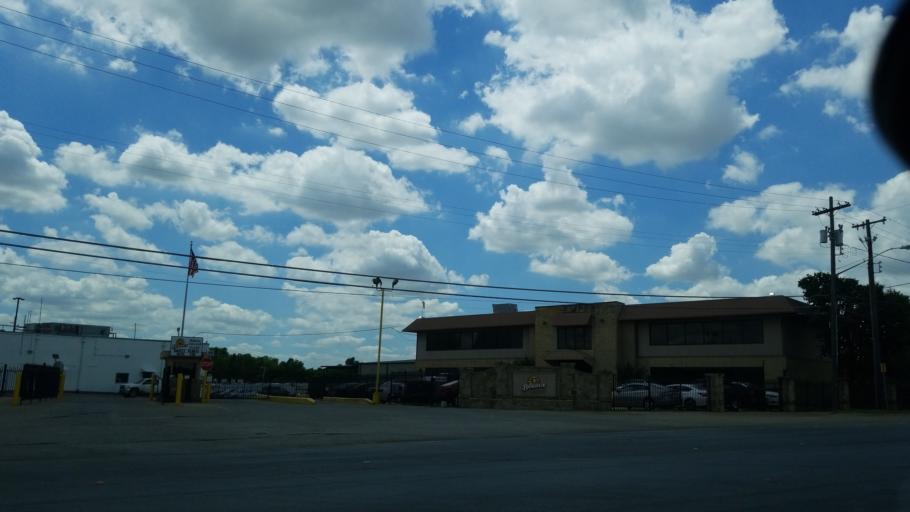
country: US
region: Texas
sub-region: Dallas County
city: Dallas
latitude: 32.7428
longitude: -96.7588
